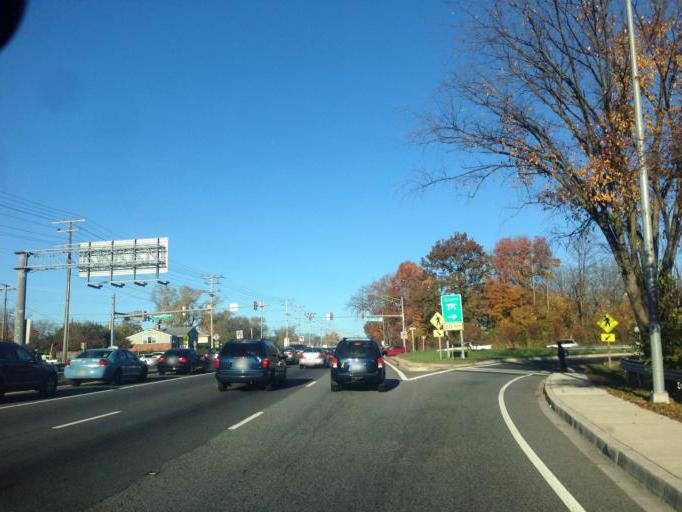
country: US
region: Maryland
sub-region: Baltimore County
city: Milford Mill
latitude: 39.3497
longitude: -76.7465
